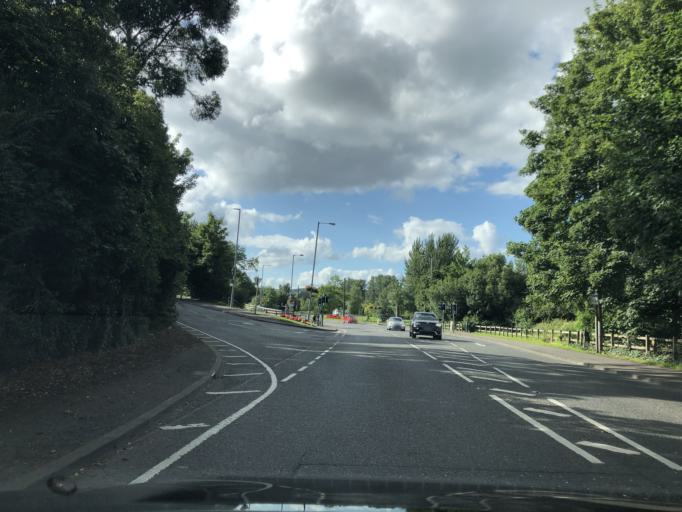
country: GB
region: Northern Ireland
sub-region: Castlereagh District
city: Dundonald
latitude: 54.5857
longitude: -5.7991
